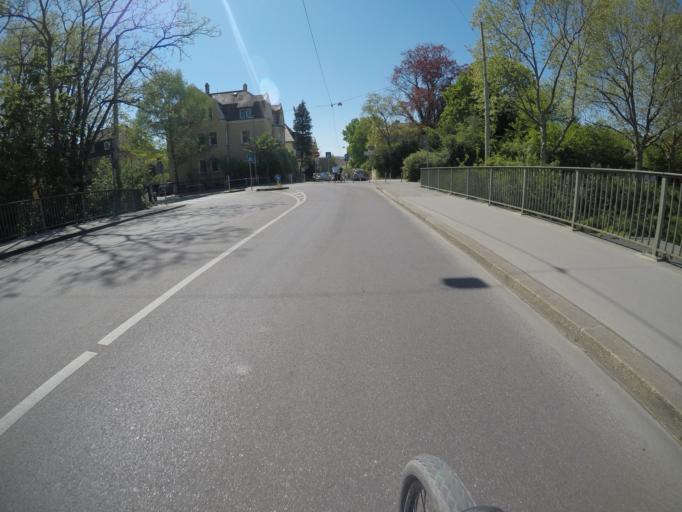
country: DE
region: Baden-Wuerttemberg
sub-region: Regierungsbezirk Stuttgart
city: Stuttgart-Ost
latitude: 48.8075
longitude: 9.2293
